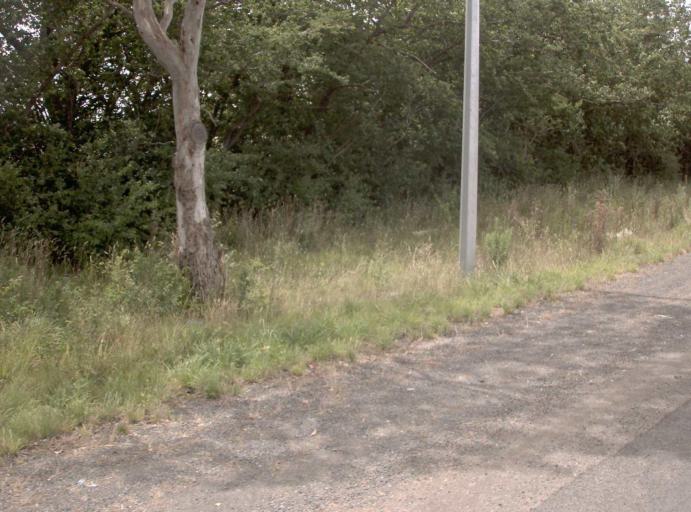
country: AU
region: Victoria
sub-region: Wellington
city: Sale
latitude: -38.0847
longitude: 147.0568
